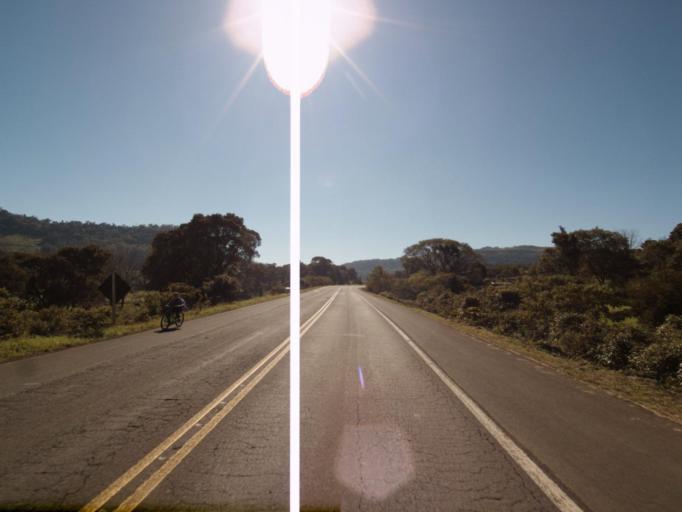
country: BR
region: Rio Grande do Sul
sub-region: Frederico Westphalen
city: Frederico Westphalen
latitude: -26.9829
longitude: -53.2217
